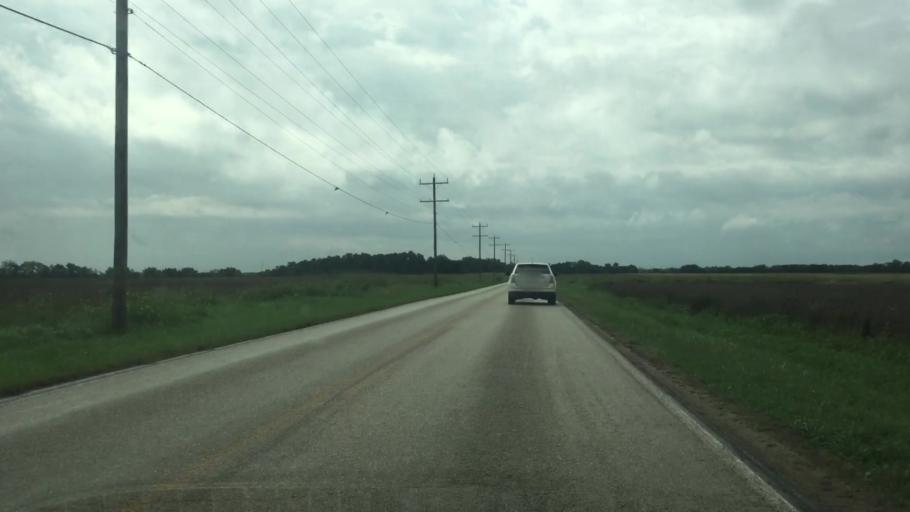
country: US
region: Kansas
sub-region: Allen County
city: Humboldt
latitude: 37.8477
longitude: -95.4369
